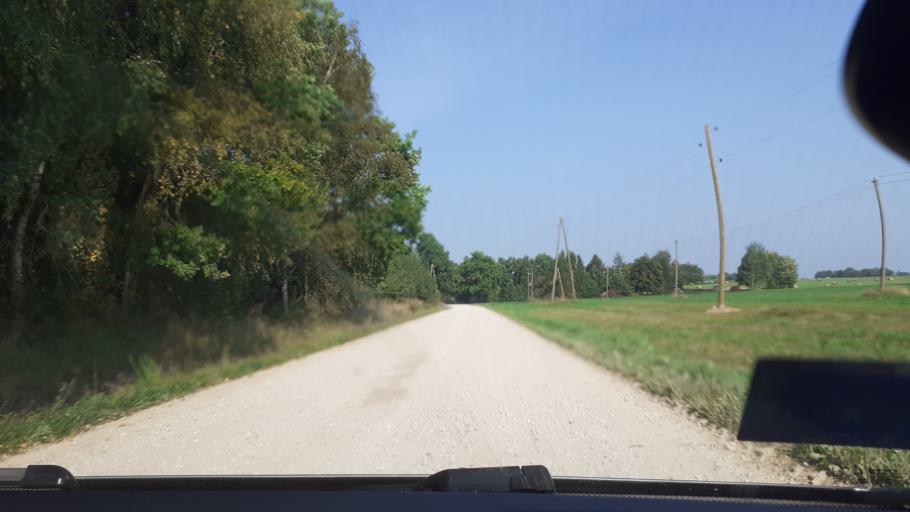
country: LV
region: Kuldigas Rajons
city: Kuldiga
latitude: 56.9918
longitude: 21.8709
